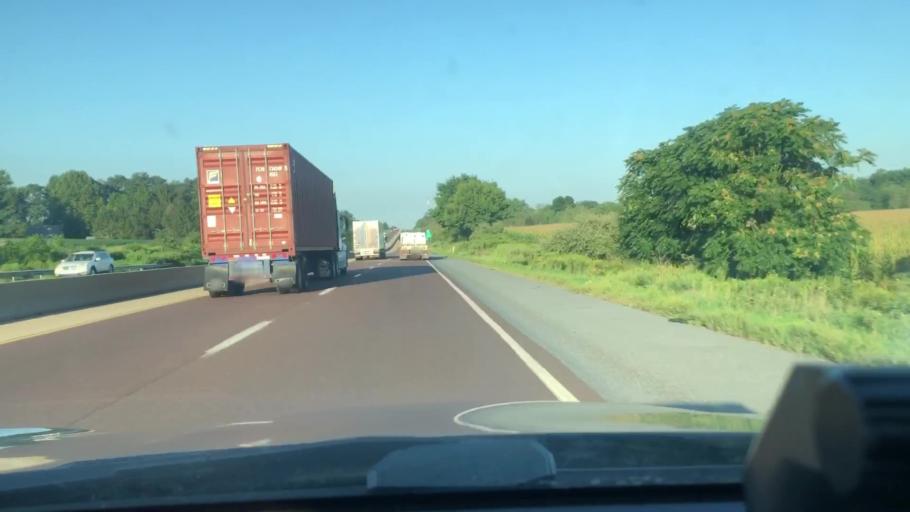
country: US
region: Pennsylvania
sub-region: Lebanon County
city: Myerstown
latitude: 40.4812
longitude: -76.2696
